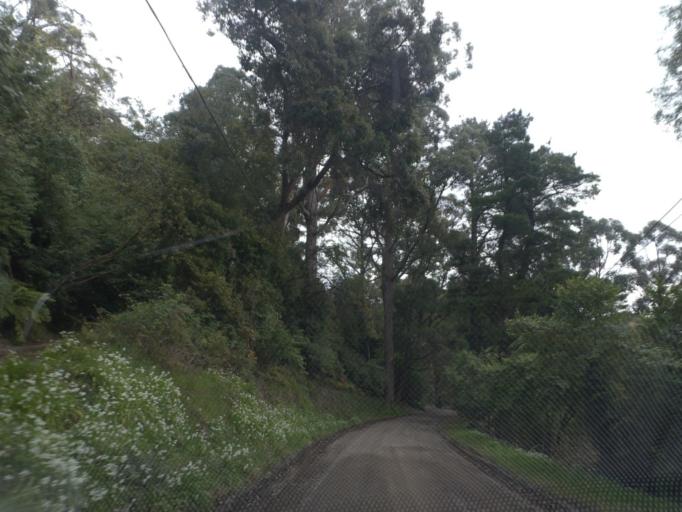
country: AU
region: Victoria
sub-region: Yarra Ranges
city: Olinda
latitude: -37.8531
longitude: 145.3579
